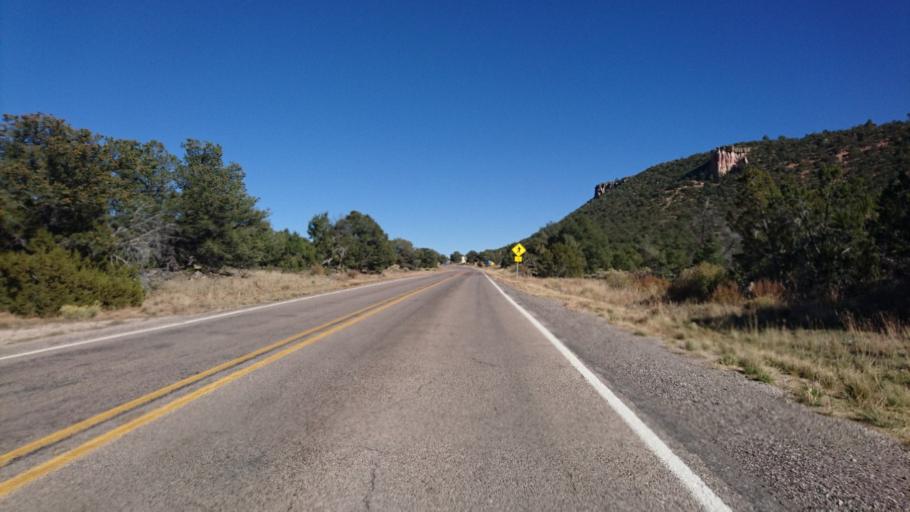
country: US
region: New Mexico
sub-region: McKinley County
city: Thoreau
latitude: 35.0437
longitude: -108.3242
